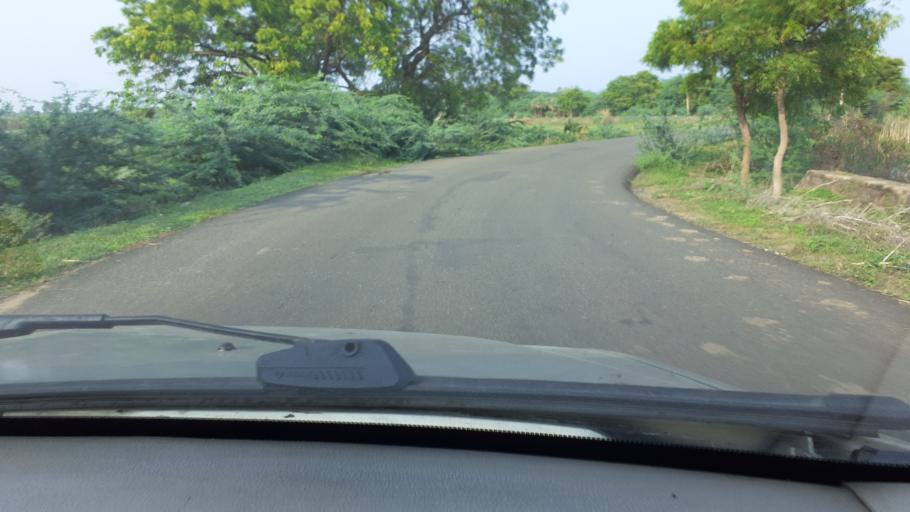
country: IN
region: Tamil Nadu
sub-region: Thoothukkudi
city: Alwar Tirunagari
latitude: 8.5814
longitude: 77.9780
